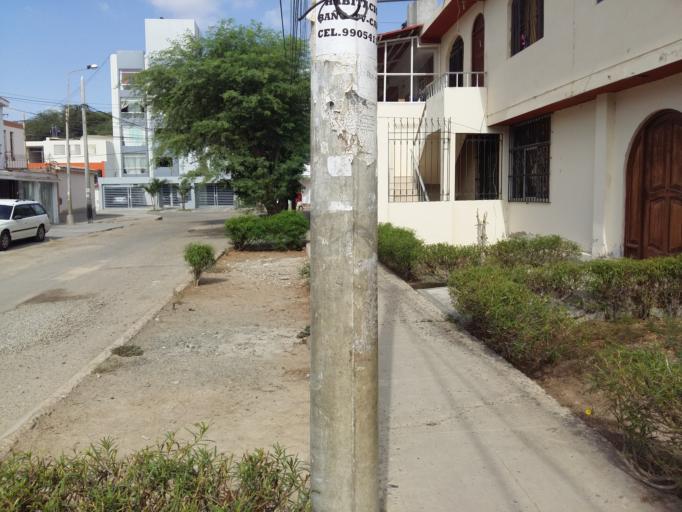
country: PE
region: Piura
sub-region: Provincia de Piura
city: Piura
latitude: -5.1904
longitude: -80.6197
